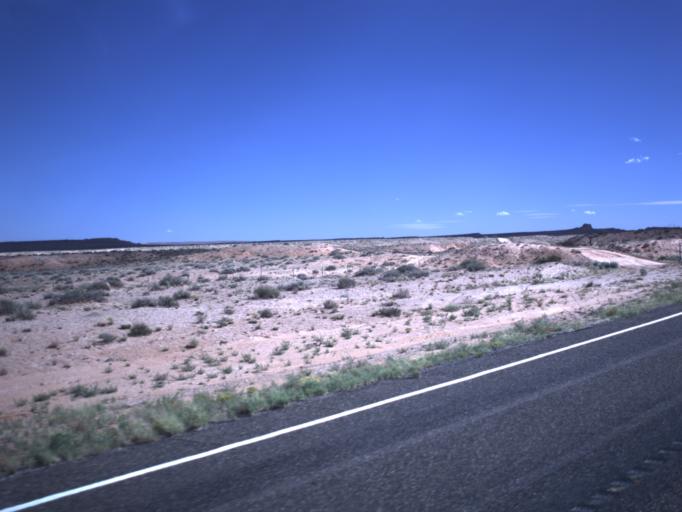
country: US
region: Utah
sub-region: Emery County
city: Ferron
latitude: 38.3036
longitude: -110.6699
